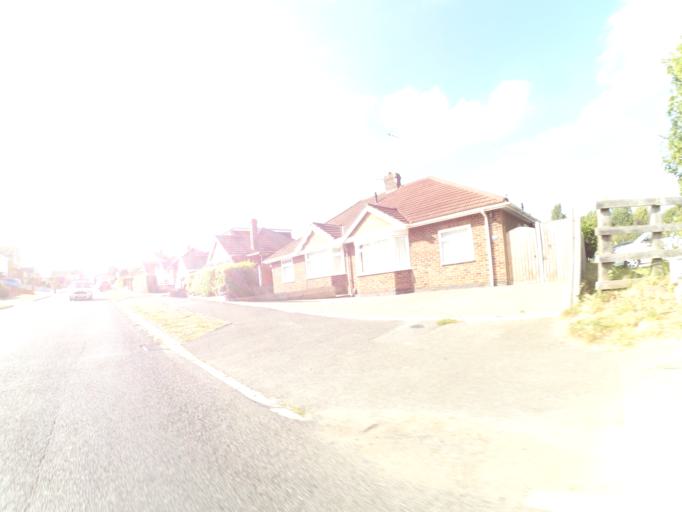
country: GB
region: England
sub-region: Warwickshire
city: Rugby
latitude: 52.3665
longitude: -1.2208
